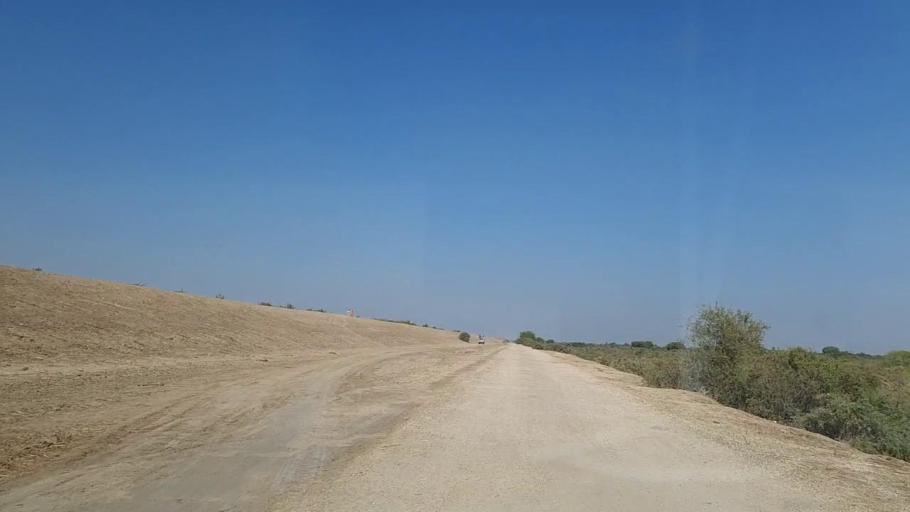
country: PK
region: Sindh
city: Chuhar Jamali
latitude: 24.4599
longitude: 68.0020
